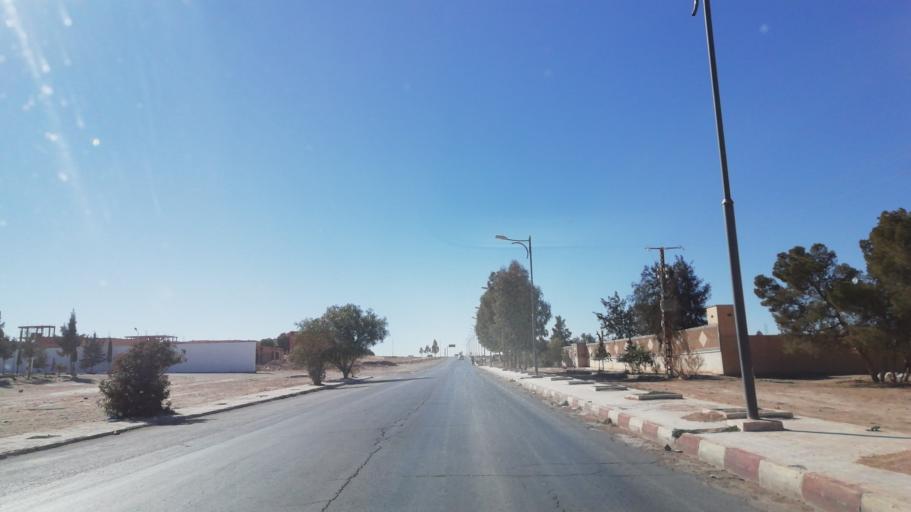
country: DZ
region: Saida
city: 'Ain el Hadjar
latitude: 34.0386
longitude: 0.0799
